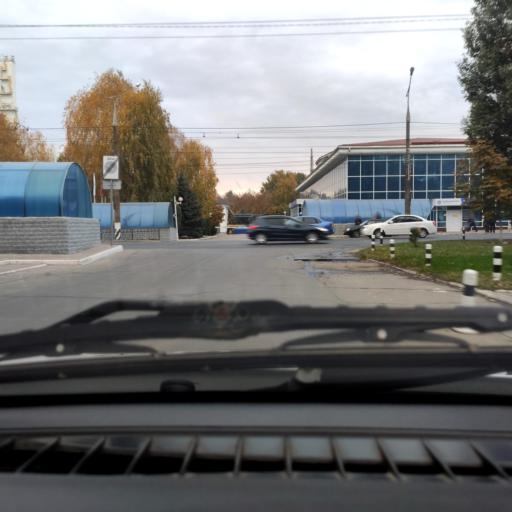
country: RU
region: Samara
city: Tol'yatti
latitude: 53.5554
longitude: 49.4508
